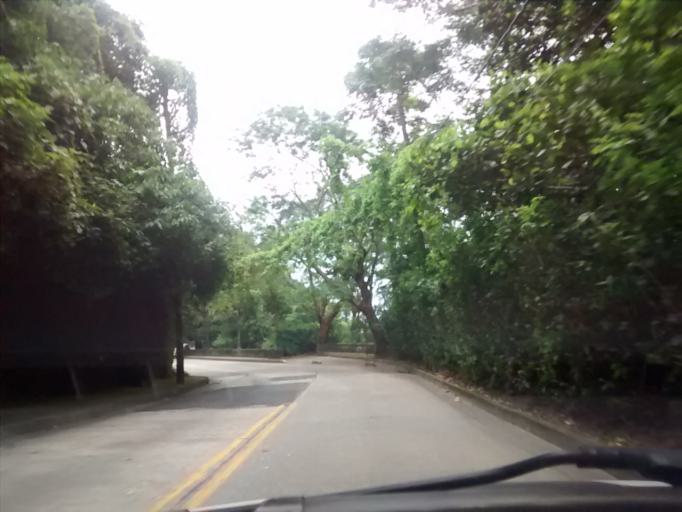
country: BR
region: Rio de Janeiro
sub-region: Rio De Janeiro
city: Rio de Janeiro
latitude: -22.9858
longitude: -43.2708
